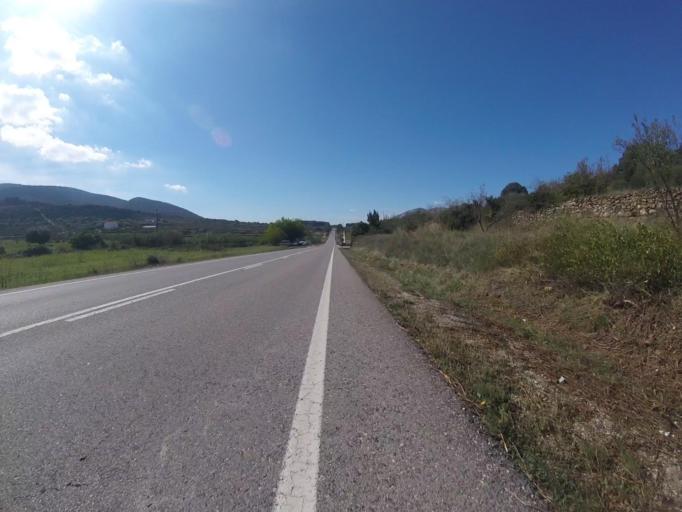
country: ES
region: Valencia
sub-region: Provincia de Castello
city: Sarratella
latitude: 40.3268
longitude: -0.0184
